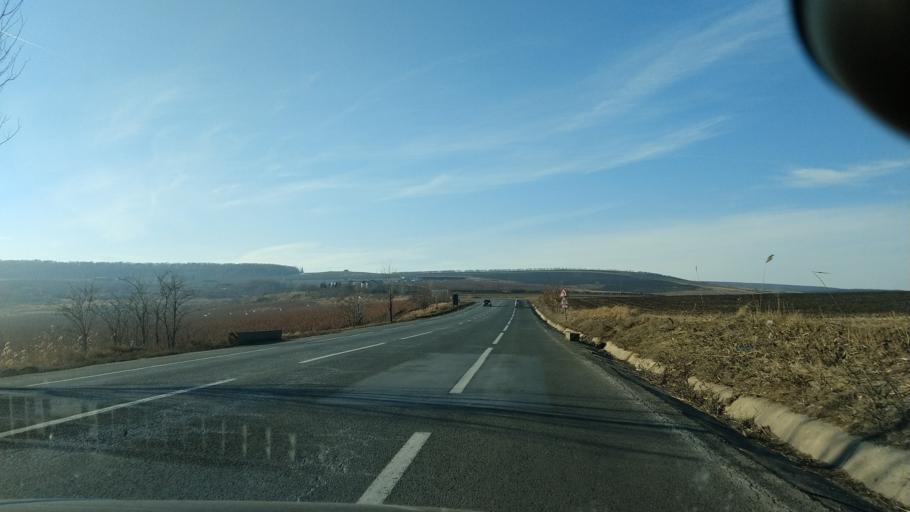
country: RO
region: Iasi
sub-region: Comuna Strunga
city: Strunga
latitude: 47.1827
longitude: 26.9664
